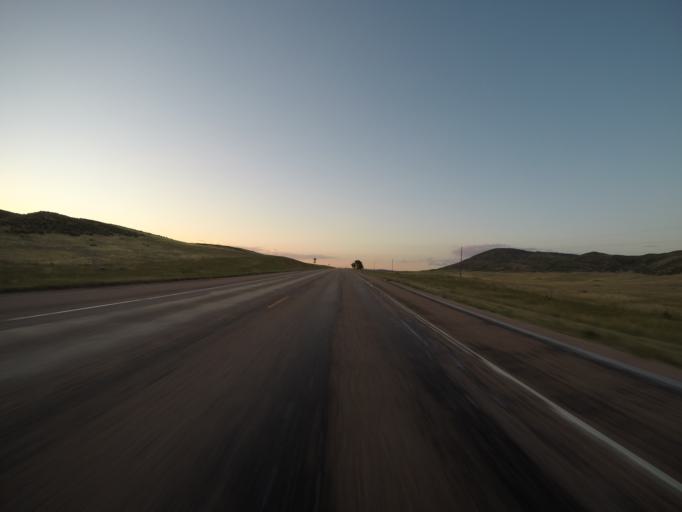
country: US
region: Colorado
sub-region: Larimer County
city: Laporte
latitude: 40.7421
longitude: -105.1707
